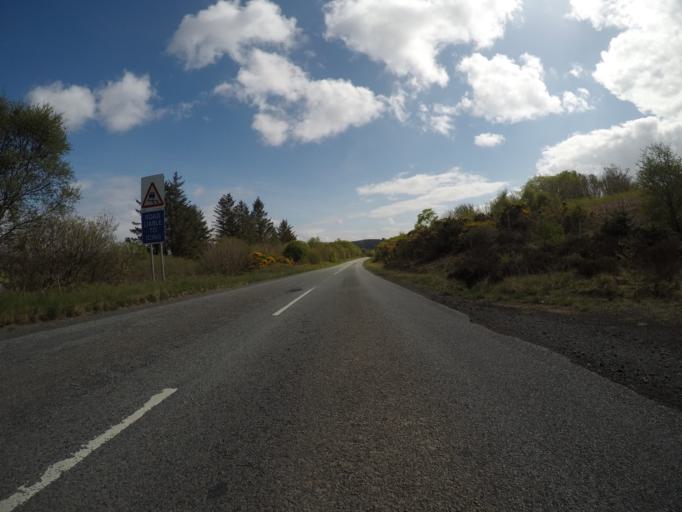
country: GB
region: Scotland
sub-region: Highland
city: Isle of Skye
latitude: 57.4626
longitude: -6.3317
